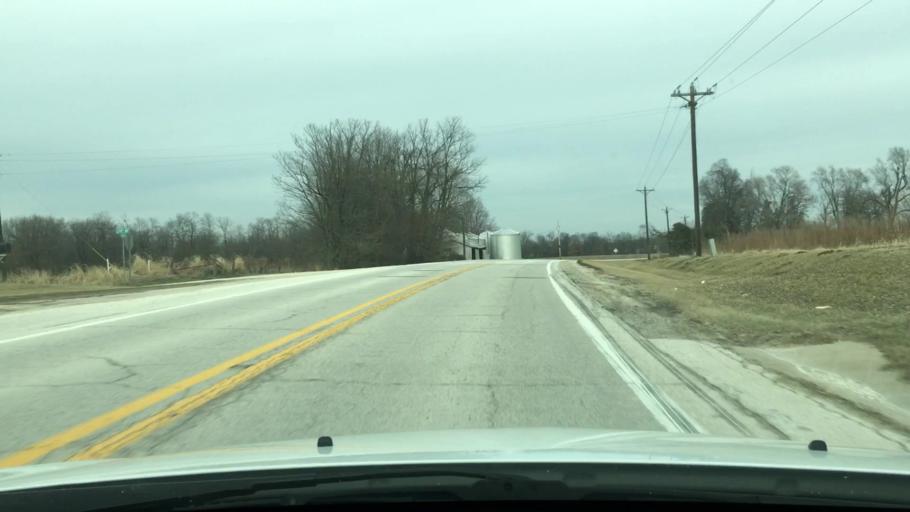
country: US
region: Illinois
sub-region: Pike County
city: Pittsfield
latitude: 39.5633
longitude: -90.9166
